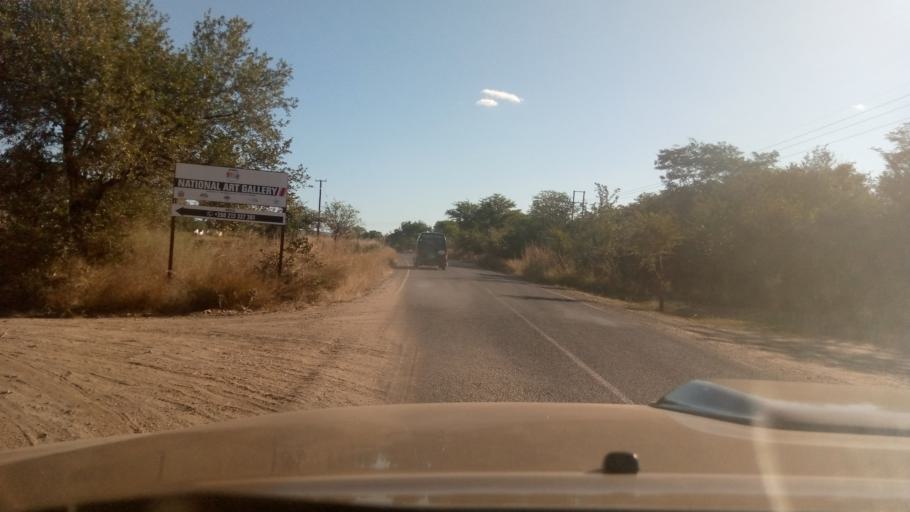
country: ZM
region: Southern
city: Livingstone
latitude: -17.8782
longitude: 25.8514
